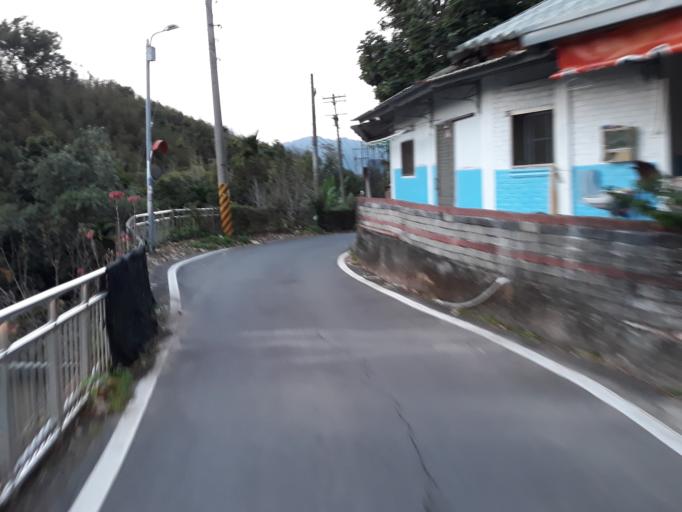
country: TW
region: Taiwan
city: Fengyuan
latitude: 24.3589
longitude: 120.8664
